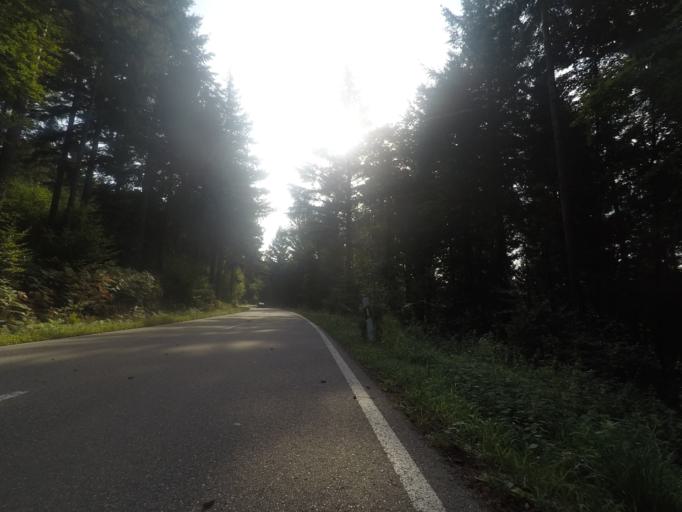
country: DE
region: Baden-Wuerttemberg
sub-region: Karlsruhe Region
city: Malsch
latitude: 48.8523
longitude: 8.3529
